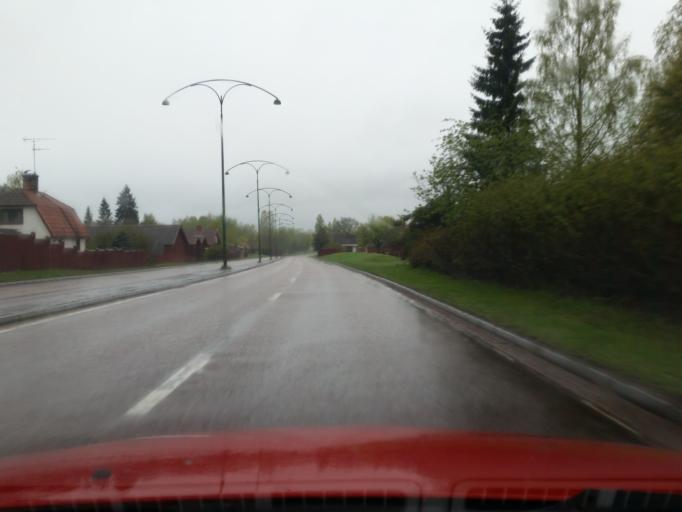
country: SE
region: Dalarna
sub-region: Borlange Kommun
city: Borlaenge
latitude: 60.5000
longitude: 15.3944
